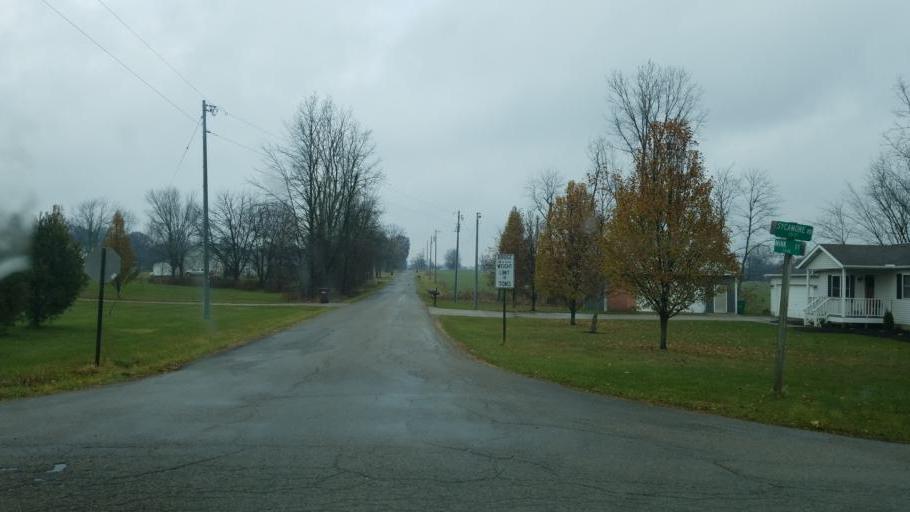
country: US
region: Ohio
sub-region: Knox County
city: Mount Vernon
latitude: 40.3160
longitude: -82.5710
